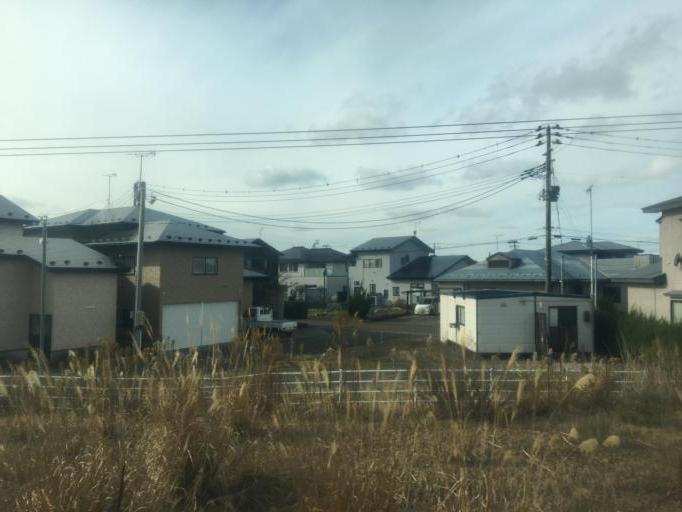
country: JP
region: Akita
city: Tenno
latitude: 39.9457
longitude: 140.0791
